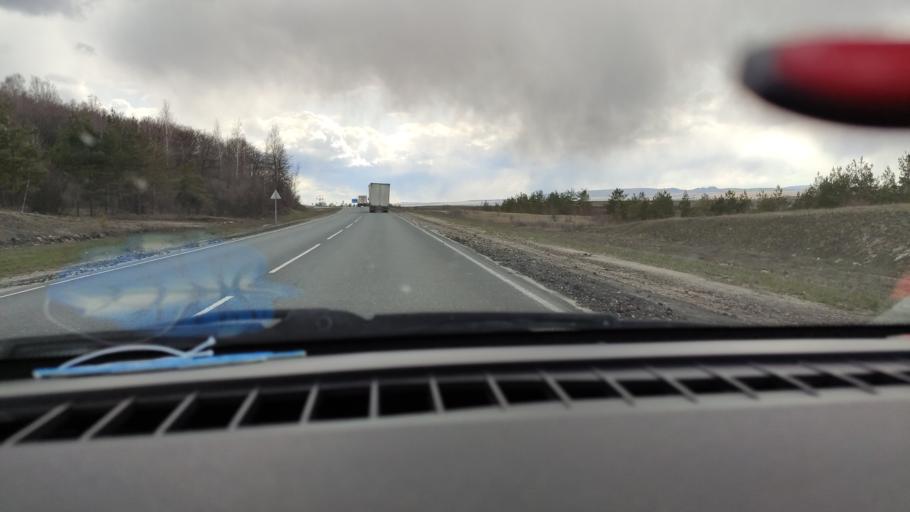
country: RU
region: Saratov
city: Alekseyevka
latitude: 52.3903
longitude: 47.9766
